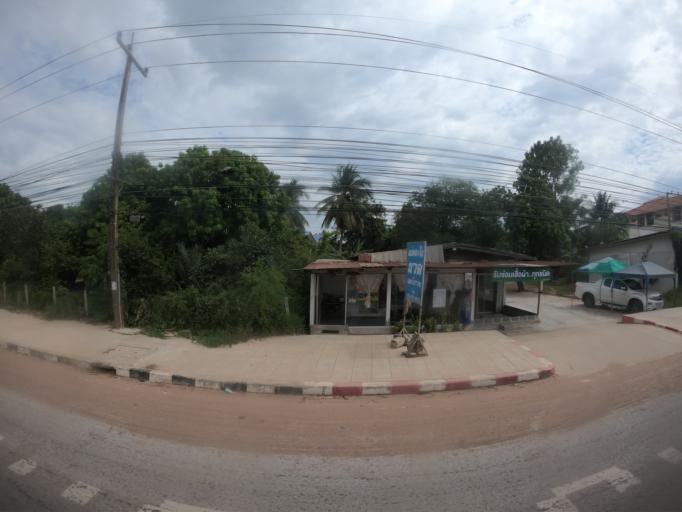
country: TH
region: Maha Sarakham
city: Maha Sarakham
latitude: 16.2377
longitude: 103.2706
